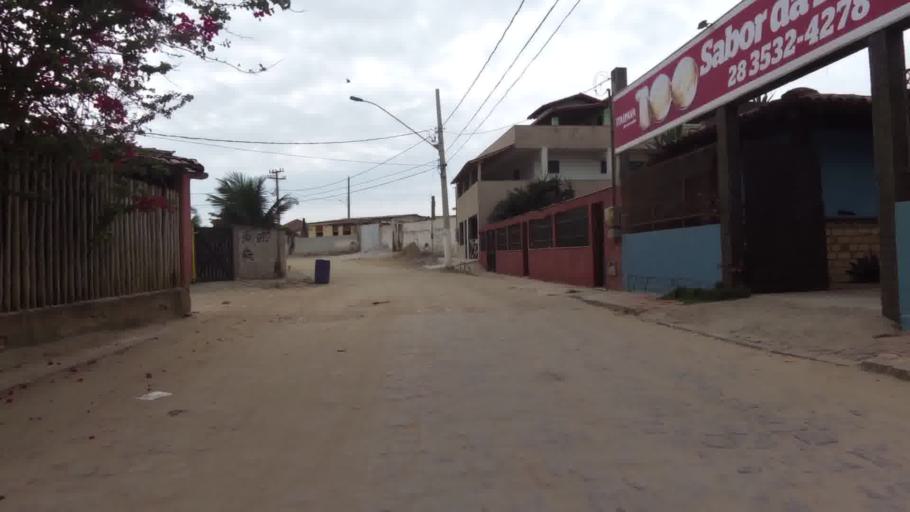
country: BR
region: Espirito Santo
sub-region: Marataizes
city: Marataizes
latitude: -21.0395
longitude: -40.8195
